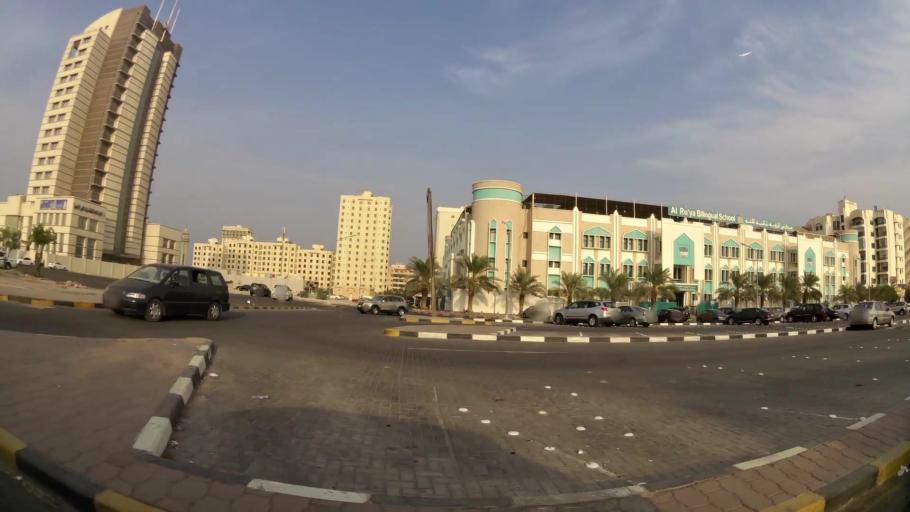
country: KW
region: Mubarak al Kabir
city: Sabah as Salim
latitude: 29.2485
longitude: 48.0812
